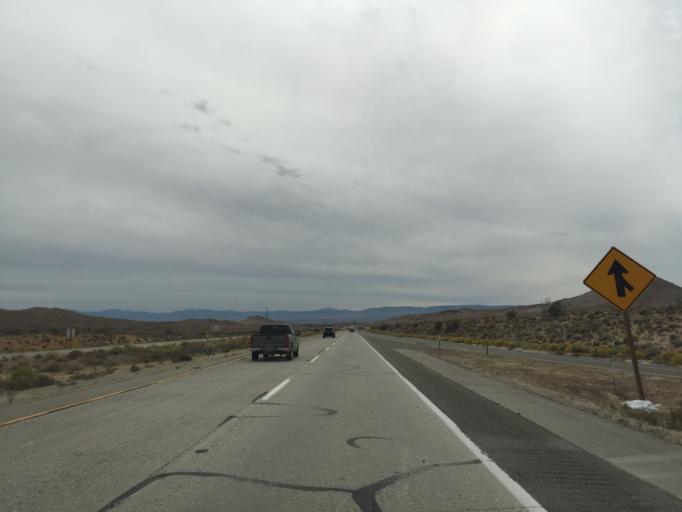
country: US
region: California
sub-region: Kern County
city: Rosamond
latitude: 34.9053
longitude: -118.1649
